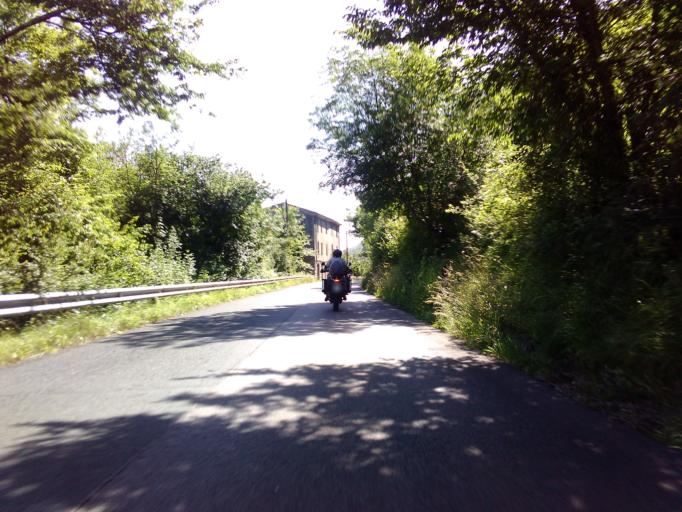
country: IT
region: Tuscany
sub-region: Provincia di Massa-Carrara
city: Licciana Nardi
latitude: 44.2792
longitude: 10.0597
